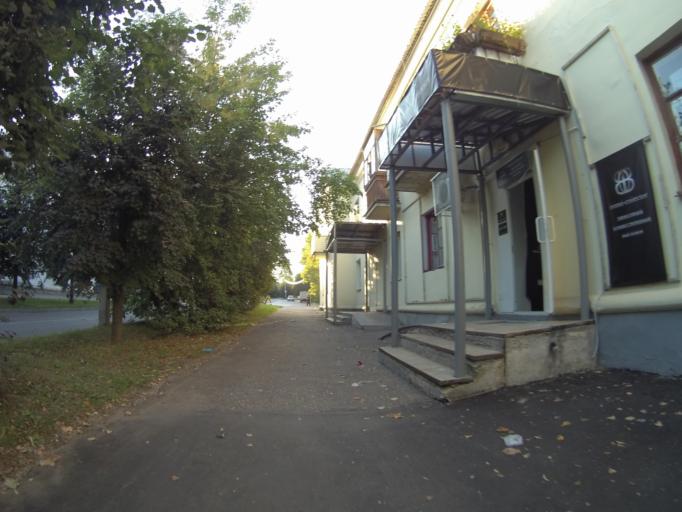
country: RU
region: Vladimir
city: Vladimir
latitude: 56.1481
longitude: 40.3842
